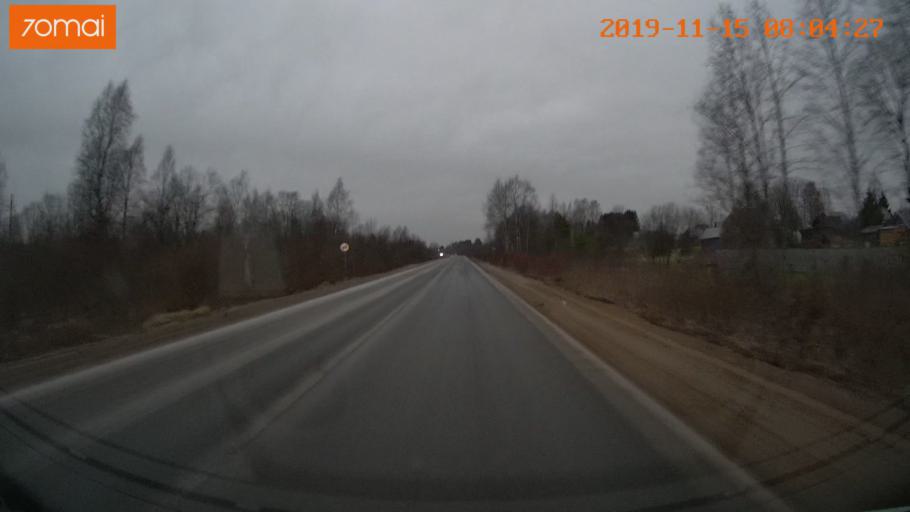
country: RU
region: Vologda
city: Cherepovets
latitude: 59.0084
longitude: 38.0758
